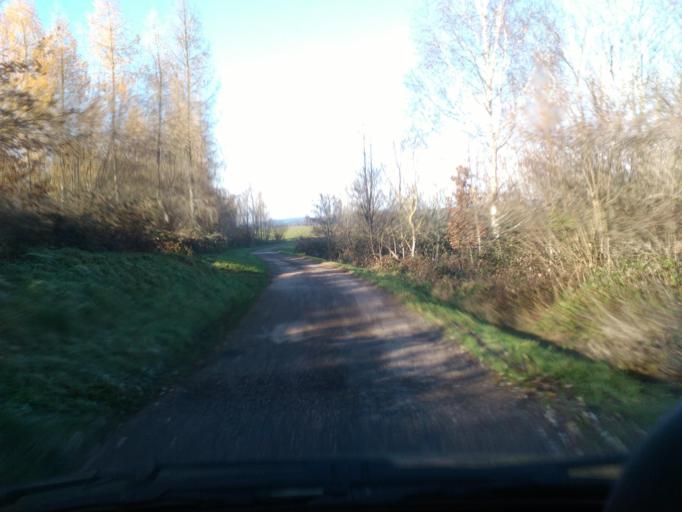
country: FR
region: Lorraine
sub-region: Departement des Vosges
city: Saint-Die-des-Vosges
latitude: 48.3324
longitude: 6.9689
